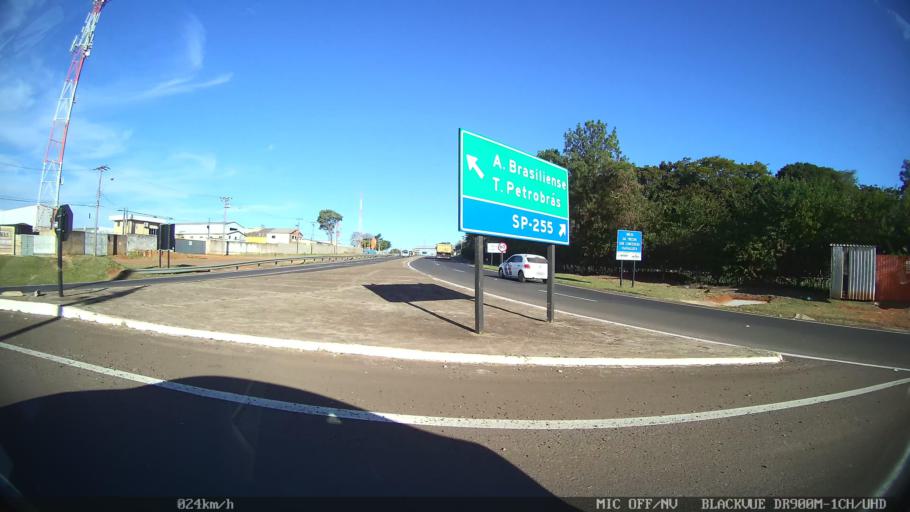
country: BR
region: Sao Paulo
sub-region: Americo Brasiliense
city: Americo Brasiliense
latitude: -21.7450
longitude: -48.1281
